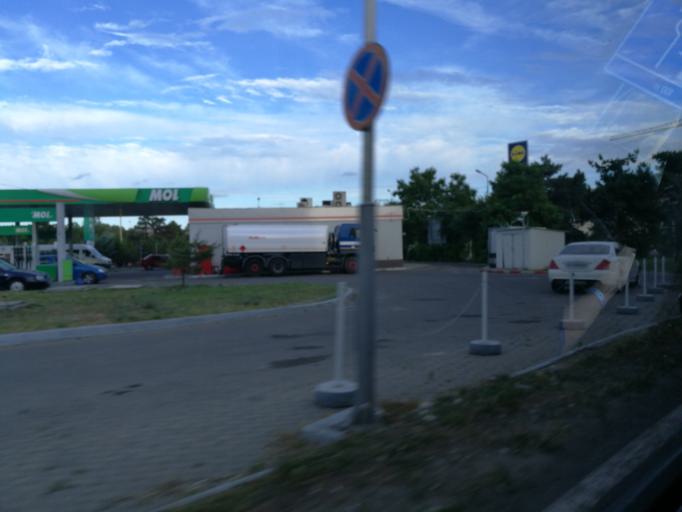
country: RO
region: Constanta
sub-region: Municipiul Constanta
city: Constanta
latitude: 44.1457
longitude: 28.6236
